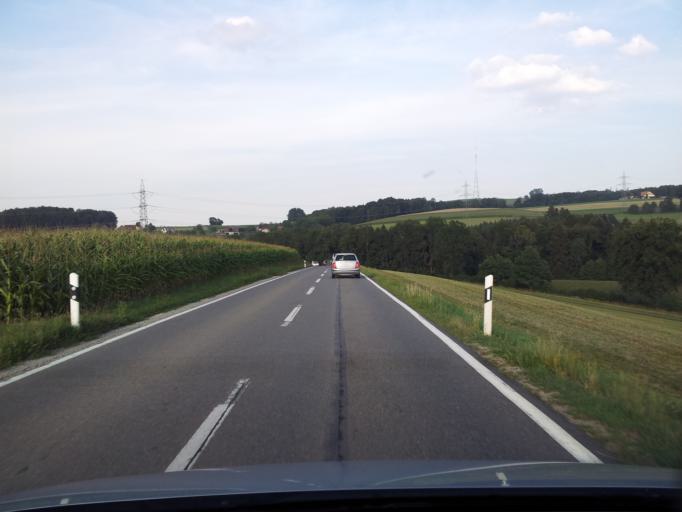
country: CH
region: Lucerne
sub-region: Sursee District
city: Schenkon
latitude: 47.1863
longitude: 8.1477
